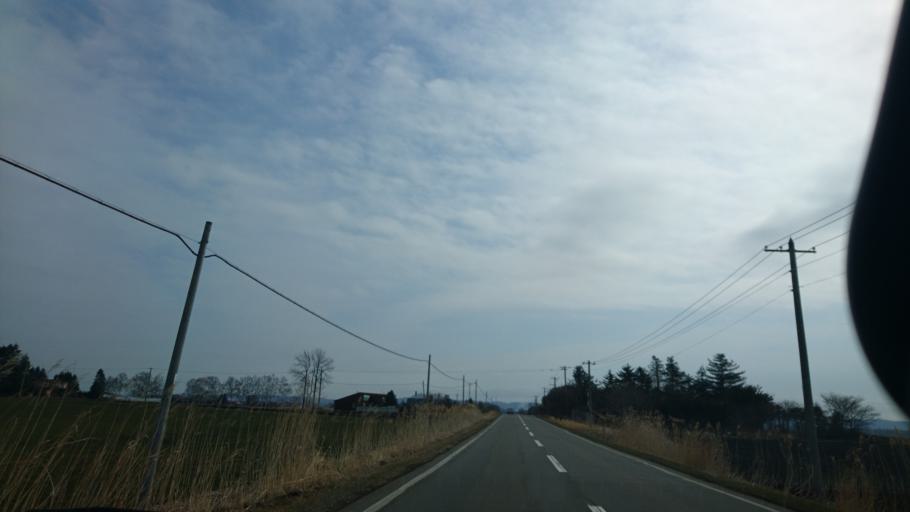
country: JP
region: Hokkaido
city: Otofuke
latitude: 43.0386
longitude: 143.2176
